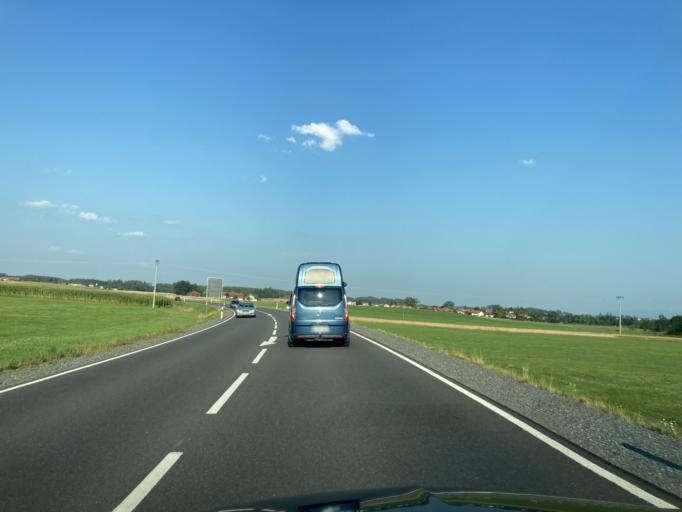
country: DE
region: Bavaria
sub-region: Upper Bavaria
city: Obing
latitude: 48.0106
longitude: 12.3941
